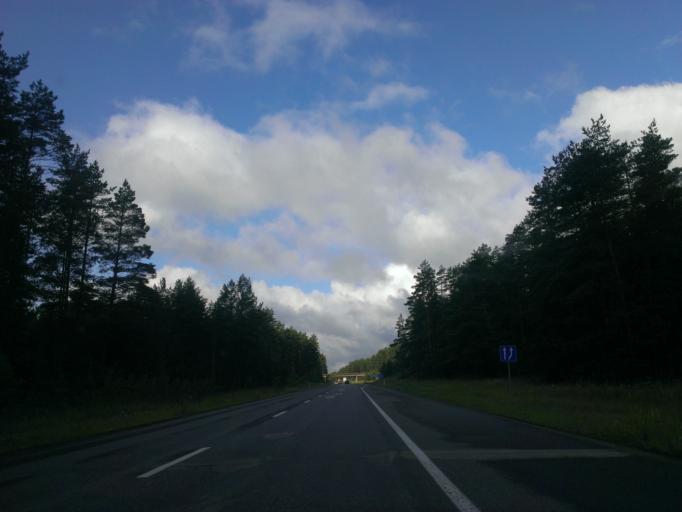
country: LV
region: Incukalns
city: Vangazi
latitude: 57.0826
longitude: 24.5278
